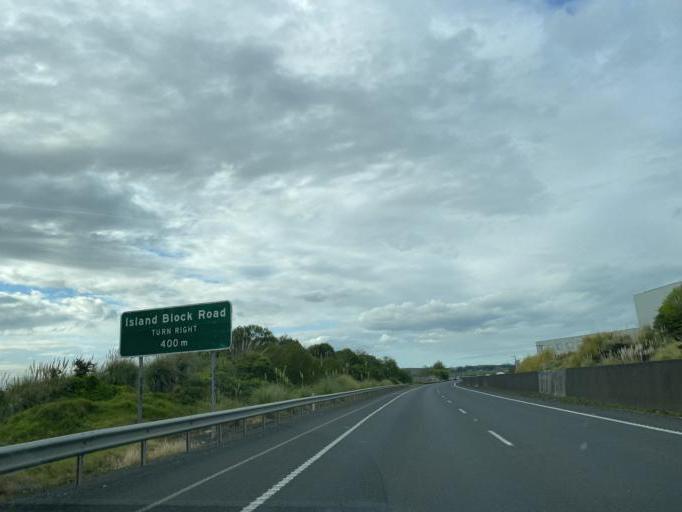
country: NZ
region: Waikato
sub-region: Waikato District
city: Te Kauwhata
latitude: -37.3157
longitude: 175.0663
